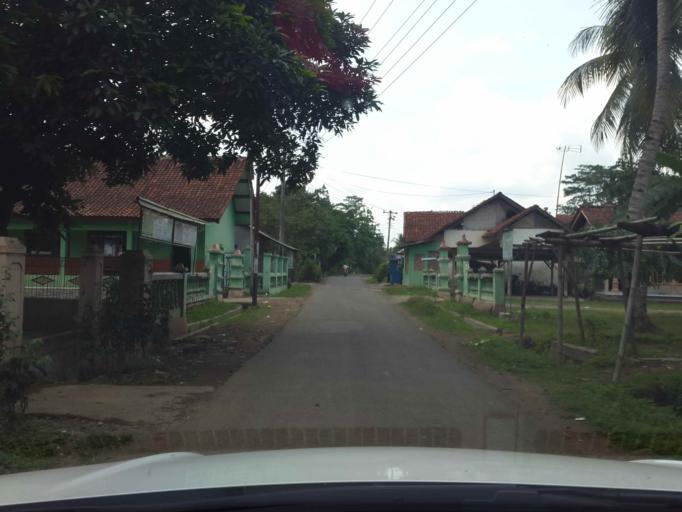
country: ID
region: Central Java
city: Bakung
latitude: -7.3499
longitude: 108.6765
